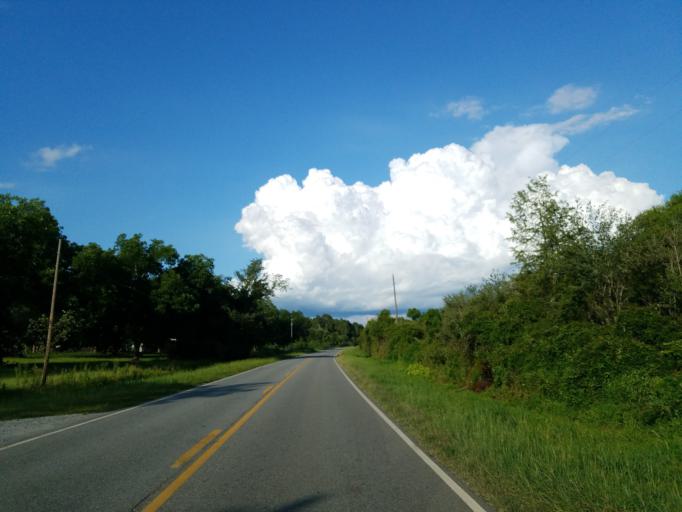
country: US
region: Georgia
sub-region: Turner County
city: Ashburn
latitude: 31.6791
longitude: -83.6291
